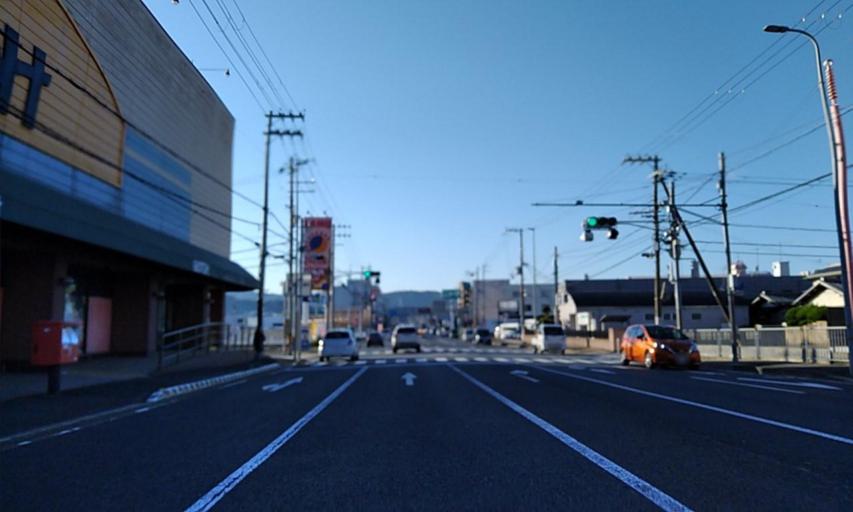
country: JP
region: Wakayama
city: Kainan
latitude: 34.1828
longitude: 135.1860
